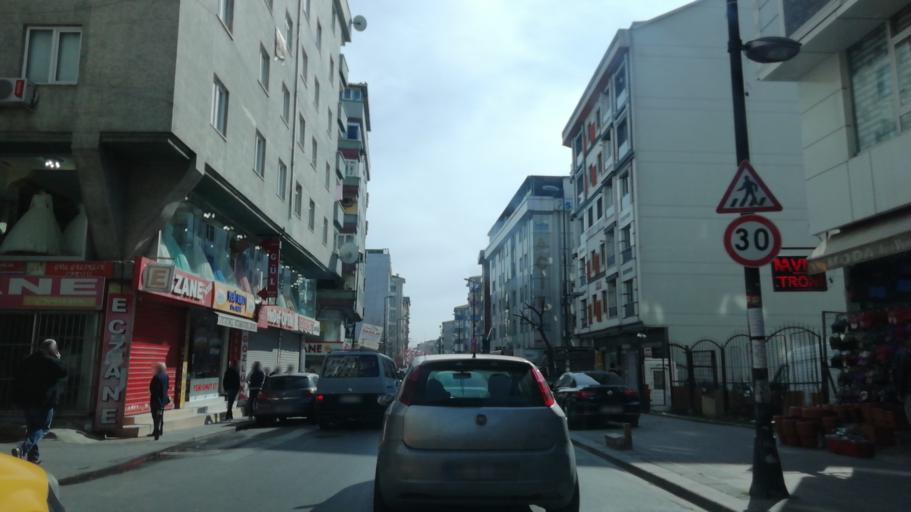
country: TR
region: Istanbul
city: Bahcelievler
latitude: 40.9999
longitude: 28.8386
